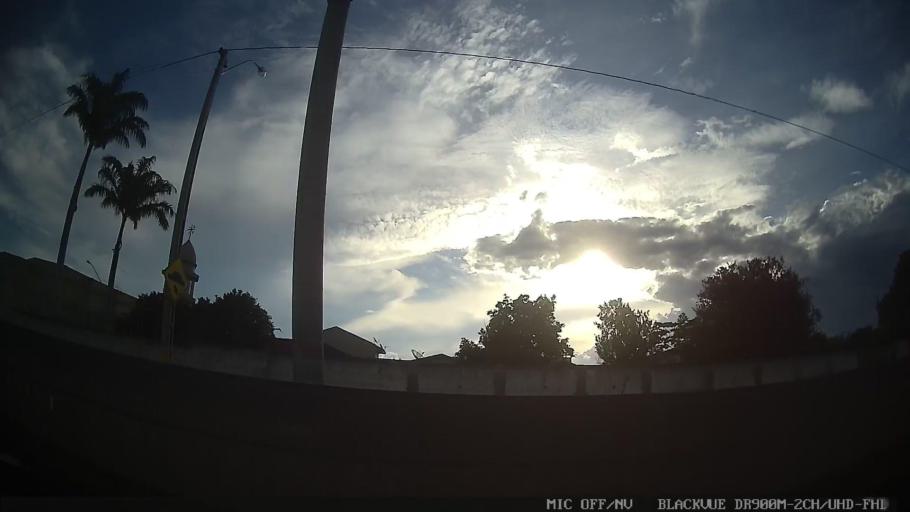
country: BR
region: Sao Paulo
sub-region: Tiete
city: Tiete
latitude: -23.0784
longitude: -47.7236
